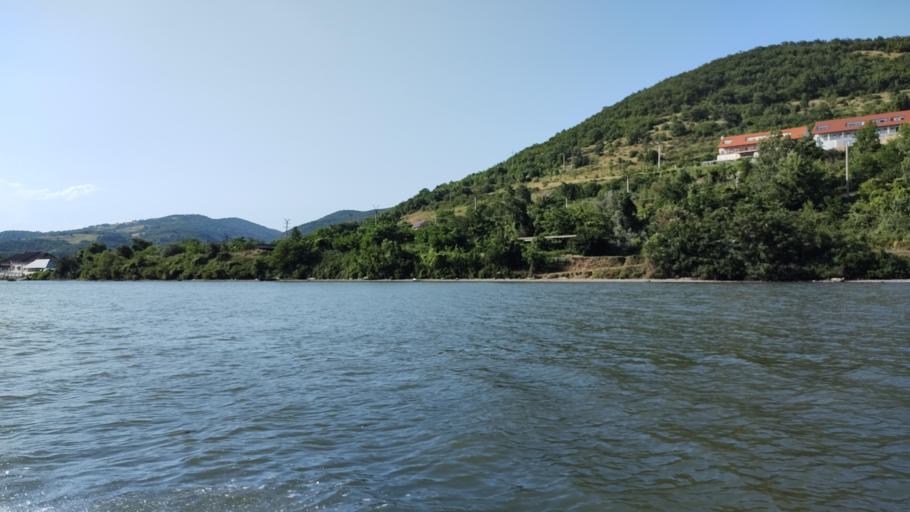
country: RO
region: Caras-Severin
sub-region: Comuna Berzasca
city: Berzasca
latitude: 44.6377
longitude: 21.9555
